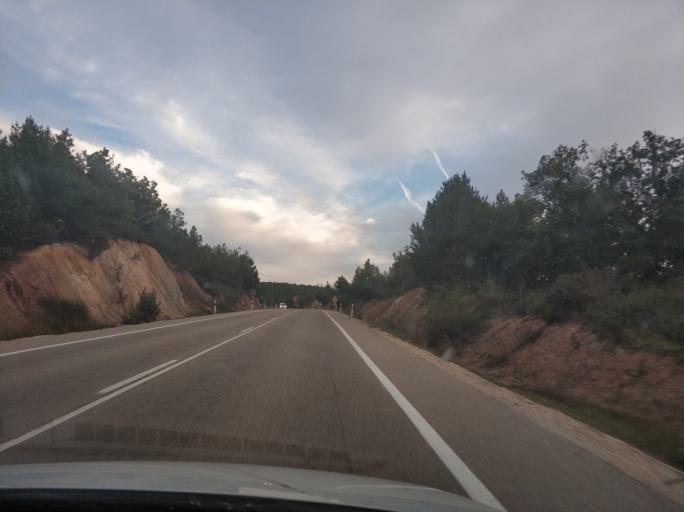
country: ES
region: Castille and Leon
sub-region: Provincia de Burgos
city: Pinilla de los Barruecos
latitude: 41.9175
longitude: -3.2795
